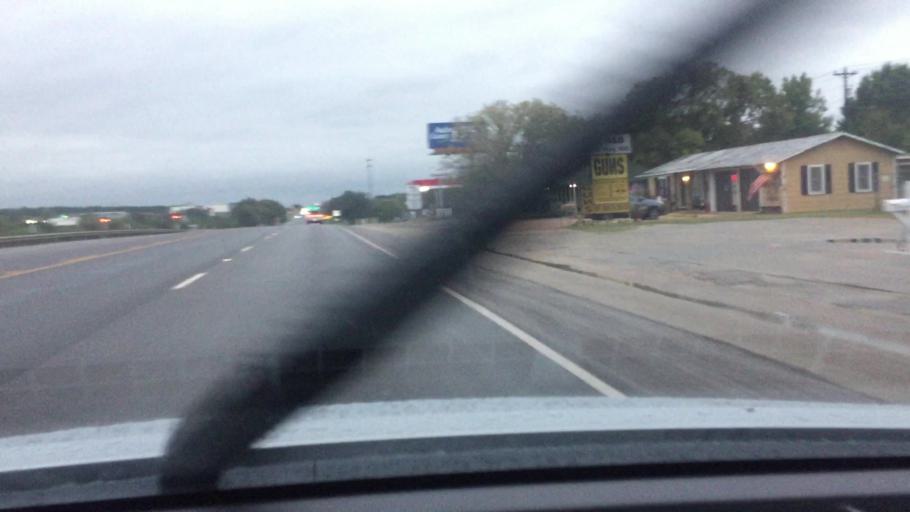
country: US
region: Texas
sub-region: Williamson County
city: Leander
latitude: 30.5766
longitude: -97.8520
